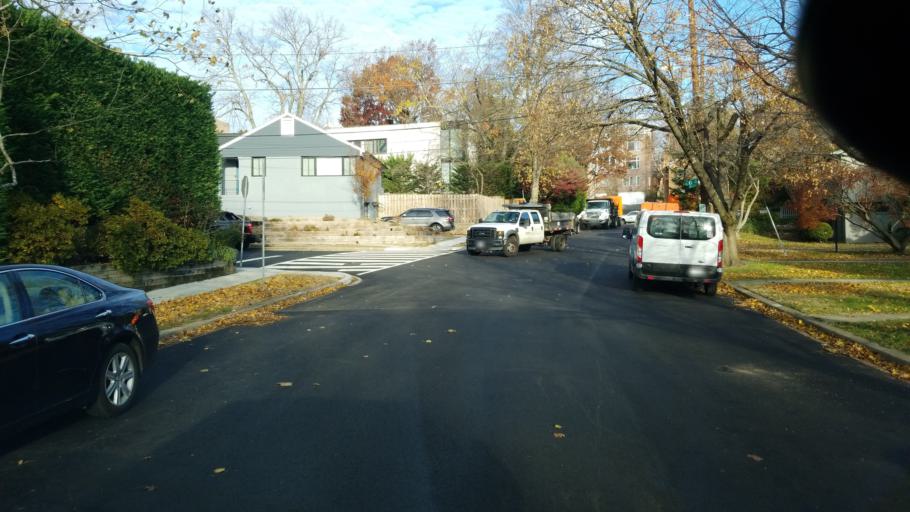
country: US
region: Virginia
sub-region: Arlington County
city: Arlington
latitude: 38.9111
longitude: -77.0859
